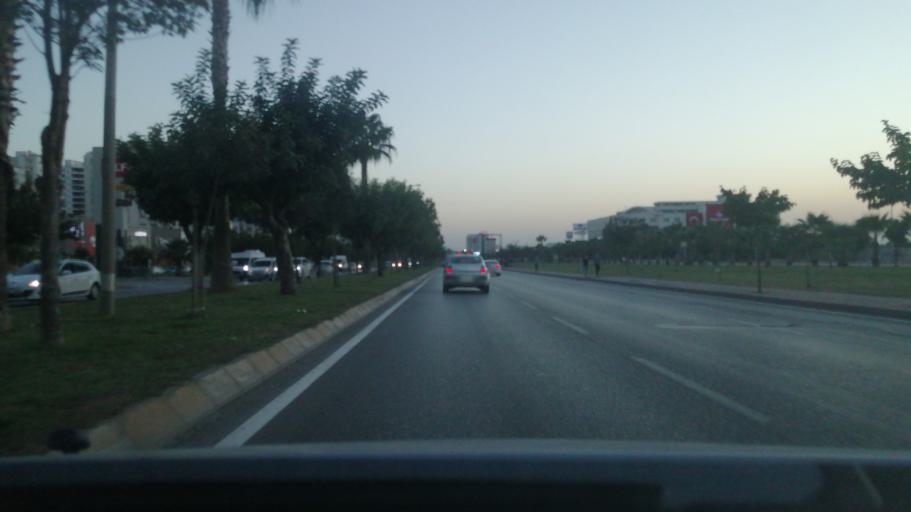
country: TR
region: Adana
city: Seyhan
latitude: 37.0212
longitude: 35.2529
